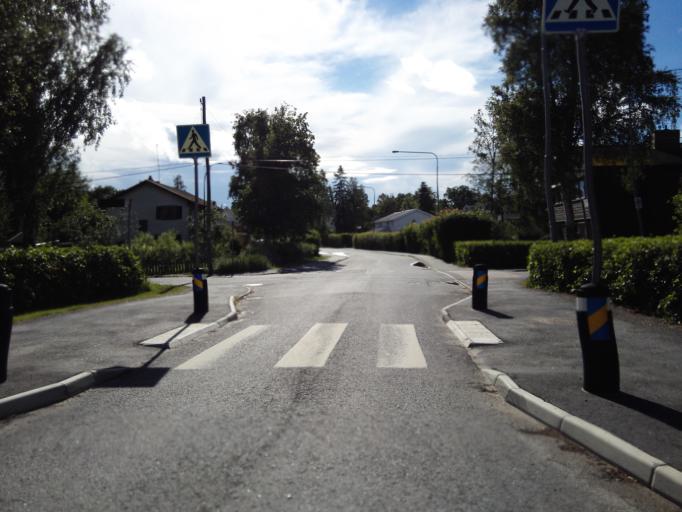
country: SE
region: Stockholm
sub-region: Huddinge Kommun
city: Huddinge
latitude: 59.2491
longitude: 17.9894
